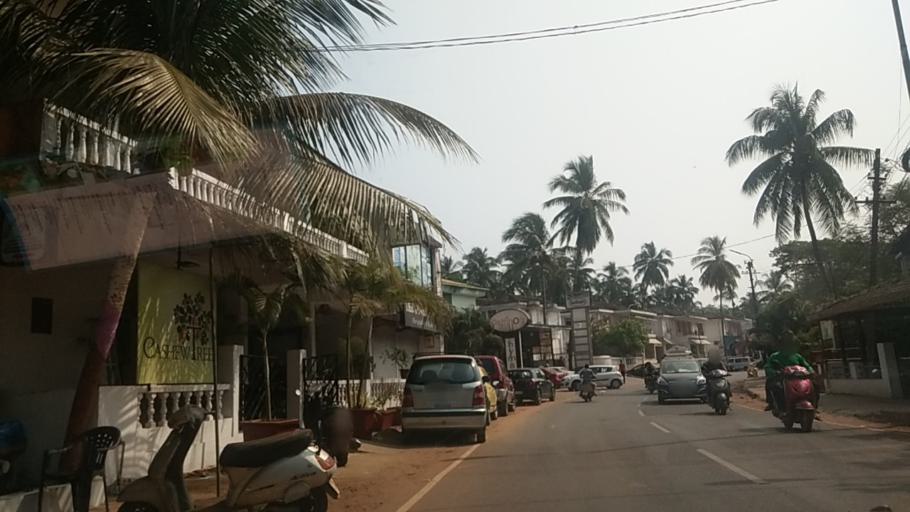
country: IN
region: Goa
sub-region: North Goa
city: Candolim
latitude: 15.5164
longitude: 73.7683
